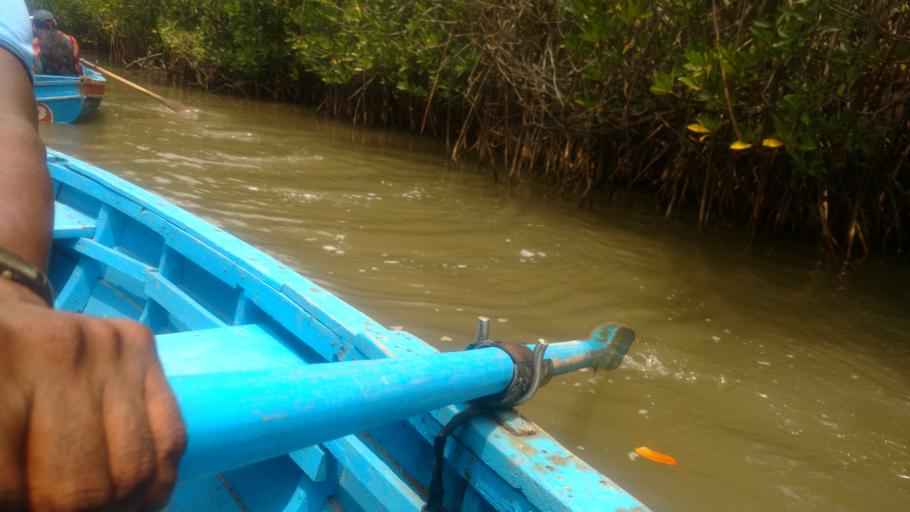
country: IN
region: Tamil Nadu
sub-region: Cuddalore
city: Annamalainagar
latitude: 11.4329
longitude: 79.7935
